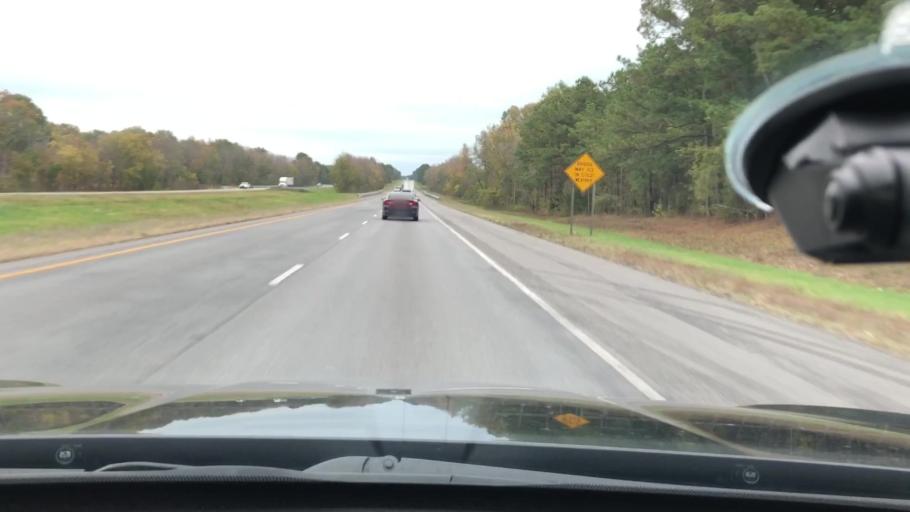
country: US
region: Arkansas
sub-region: Hempstead County
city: Hope
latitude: 33.6239
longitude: -93.7648
